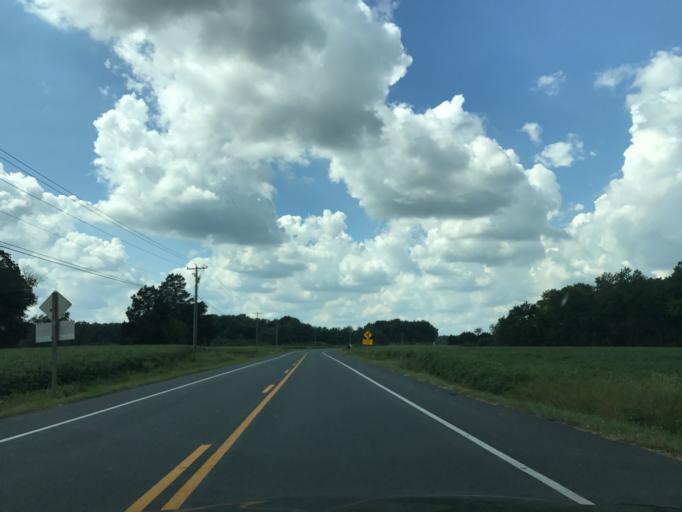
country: US
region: Maryland
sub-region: Caroline County
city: Greensboro
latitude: 39.1332
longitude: -75.7874
